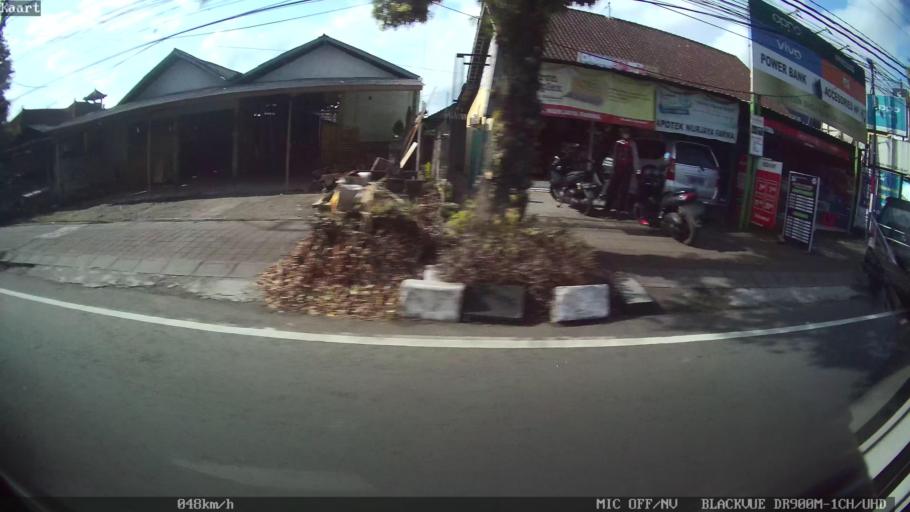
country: ID
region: Bali
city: Banjar Jumbayah
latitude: -8.5627
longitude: 115.1642
